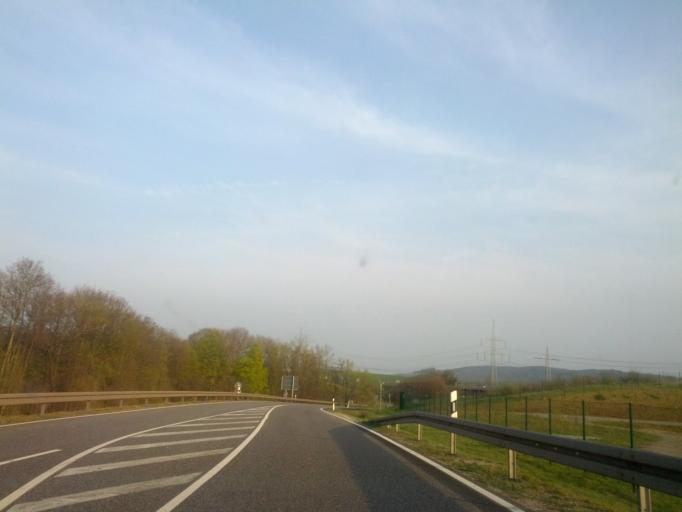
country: DE
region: Thuringia
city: Bischofroda
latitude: 51.0012
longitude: 10.4098
